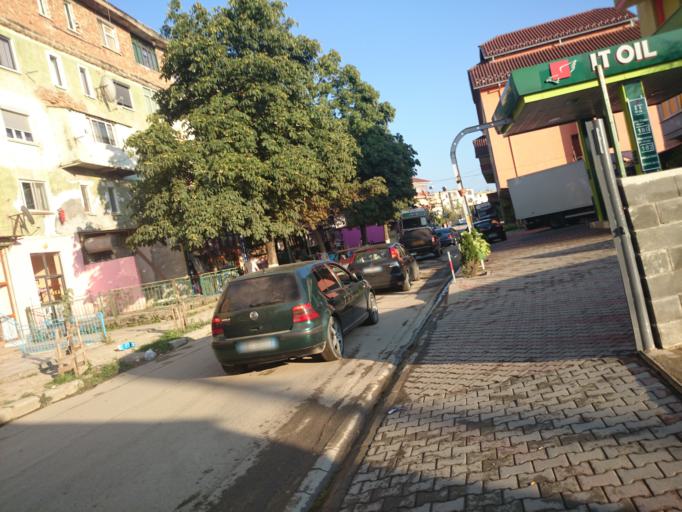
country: AL
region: Diber
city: Peshkopi
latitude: 41.6853
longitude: 20.4251
